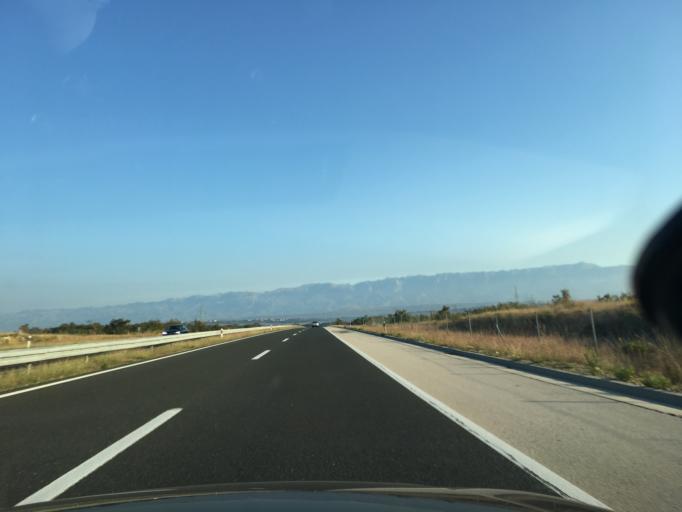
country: HR
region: Zadarska
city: Policnik
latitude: 44.1417
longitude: 15.4208
